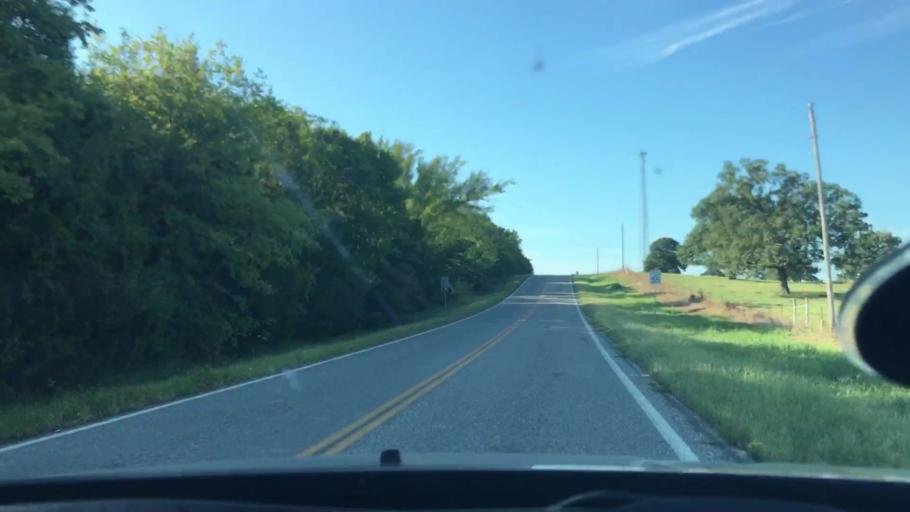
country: US
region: Oklahoma
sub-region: Coal County
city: Coalgate
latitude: 34.6175
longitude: -96.4243
